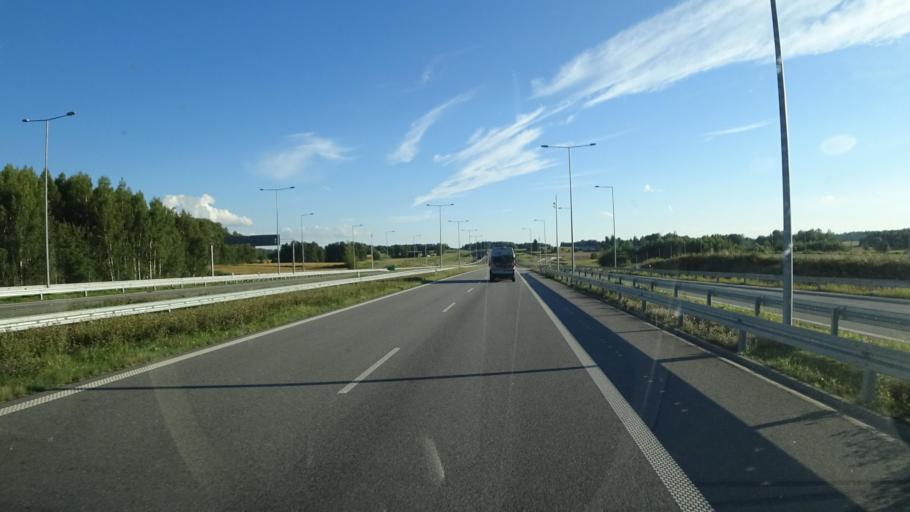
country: PL
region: Podlasie
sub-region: Powiat suwalski
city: Raczki
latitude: 53.9689
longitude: 22.7829
